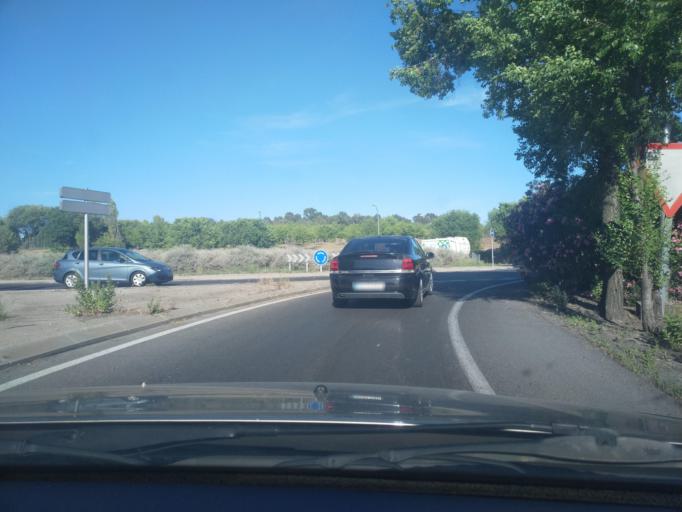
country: ES
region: Madrid
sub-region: Provincia de Madrid
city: Vicalvaro
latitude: 40.3919
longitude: -3.6192
